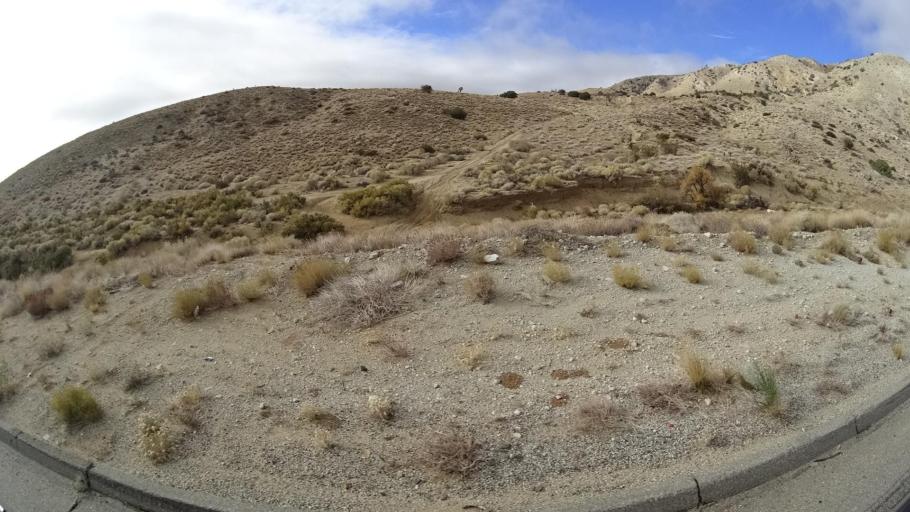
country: US
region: California
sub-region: Kern County
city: Tehachapi
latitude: 35.0131
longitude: -118.3450
